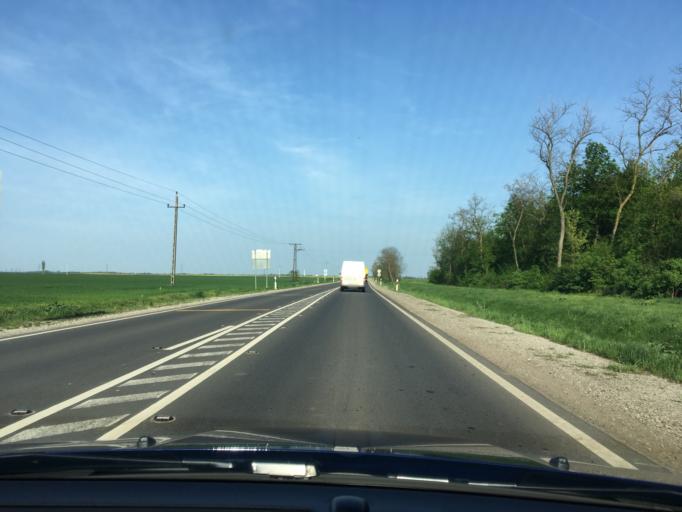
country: HU
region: Bekes
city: Ujkigyos
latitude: 46.6631
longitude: 20.9558
